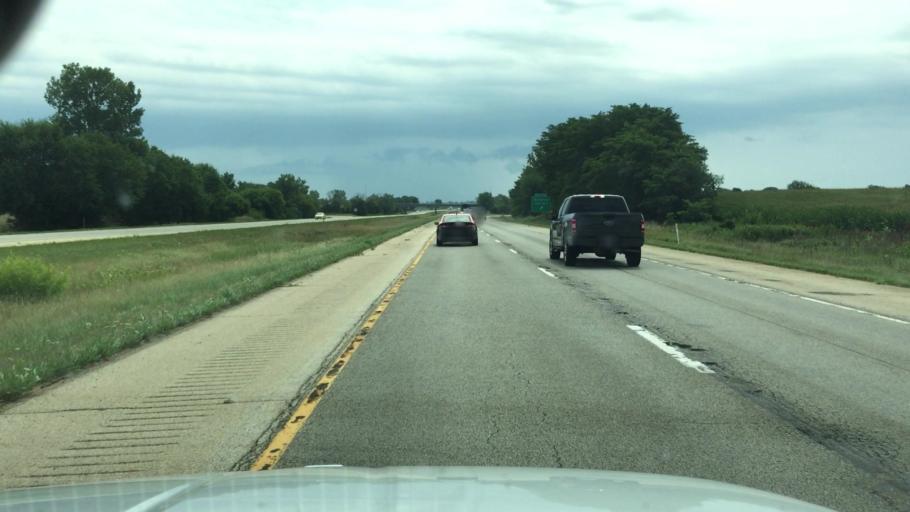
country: US
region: Illinois
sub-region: Peoria County
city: Elmwood
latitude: 40.8302
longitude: -89.8775
